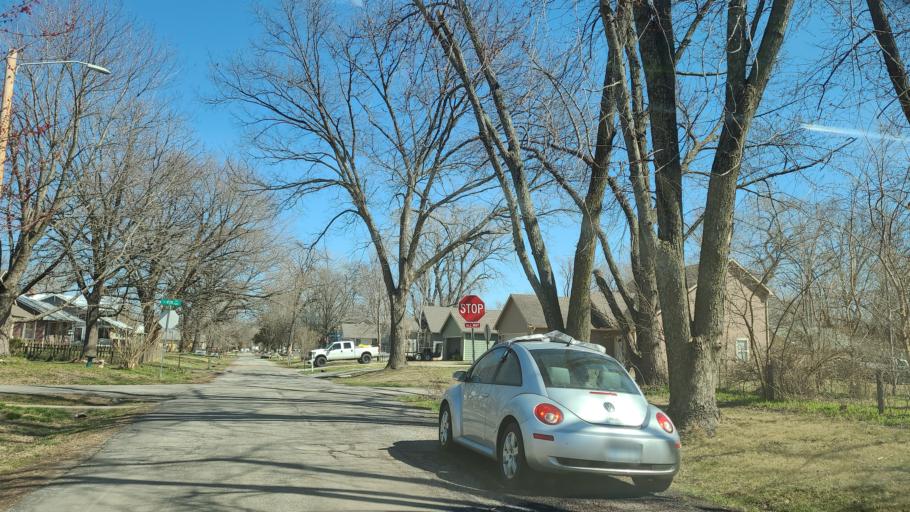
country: US
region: Kansas
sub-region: Douglas County
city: Lawrence
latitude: 38.9797
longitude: -95.2315
